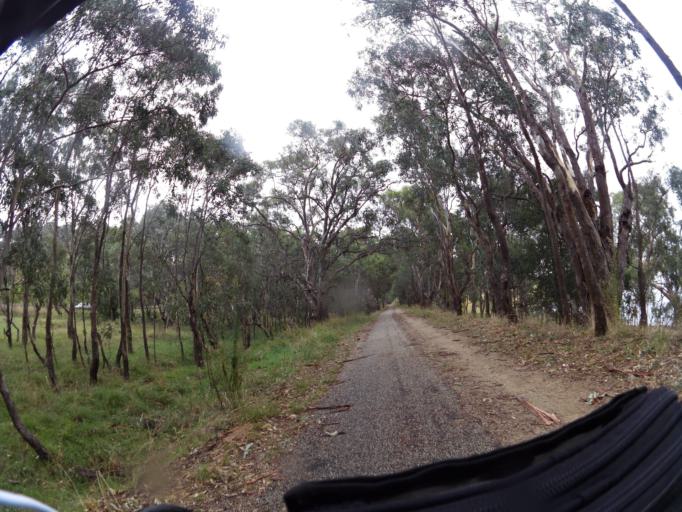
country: AU
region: New South Wales
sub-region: Albury Municipality
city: East Albury
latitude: -36.2233
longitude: 147.1303
